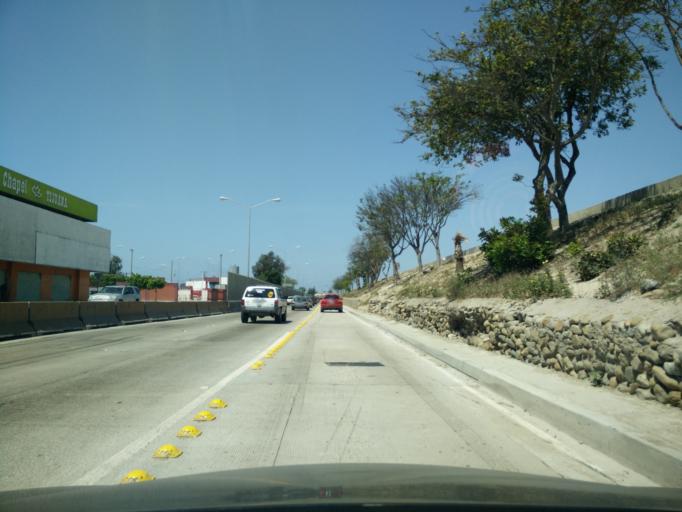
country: MX
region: Baja California
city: Tijuana
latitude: 32.5386
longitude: -117.0337
